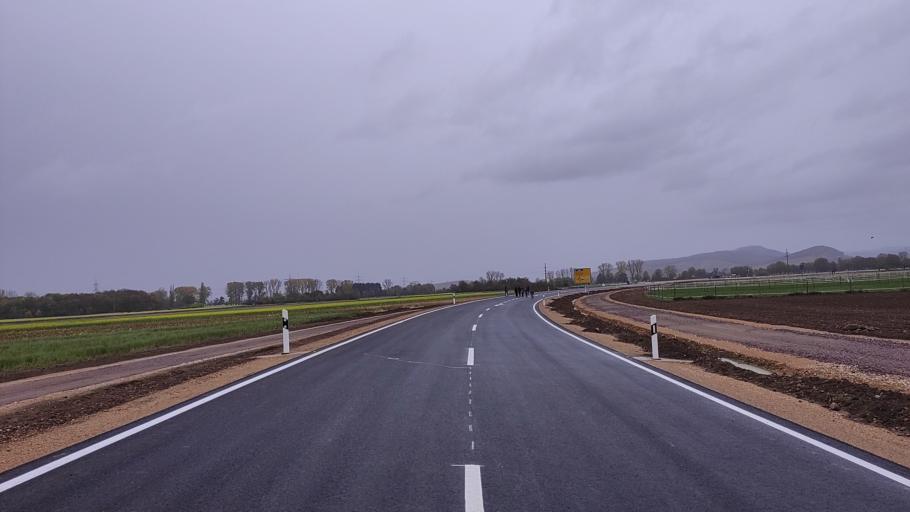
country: DE
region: Baden-Wuerttemberg
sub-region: Freiburg Region
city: Bad Krozingen
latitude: 47.8874
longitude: 7.7145
